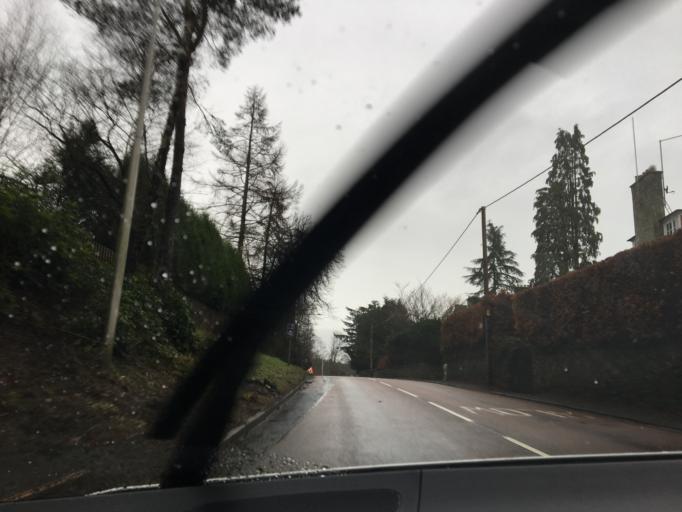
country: GB
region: Scotland
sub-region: Stirling
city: Doune
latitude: 56.1874
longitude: -4.0579
